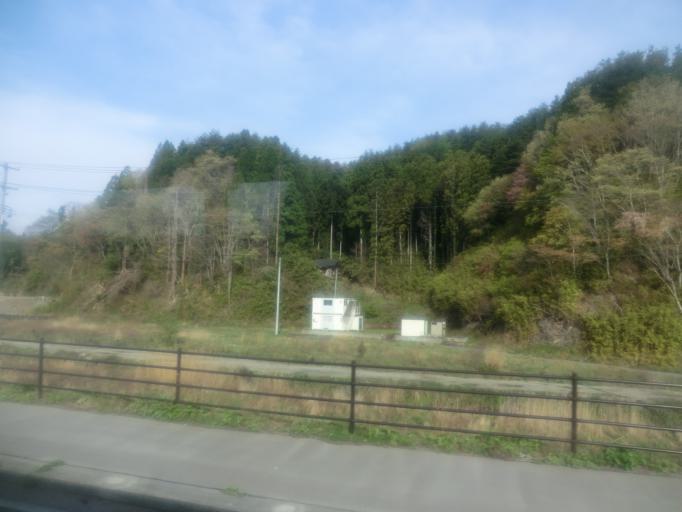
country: JP
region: Iwate
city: Miyako
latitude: 39.5869
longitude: 141.9454
